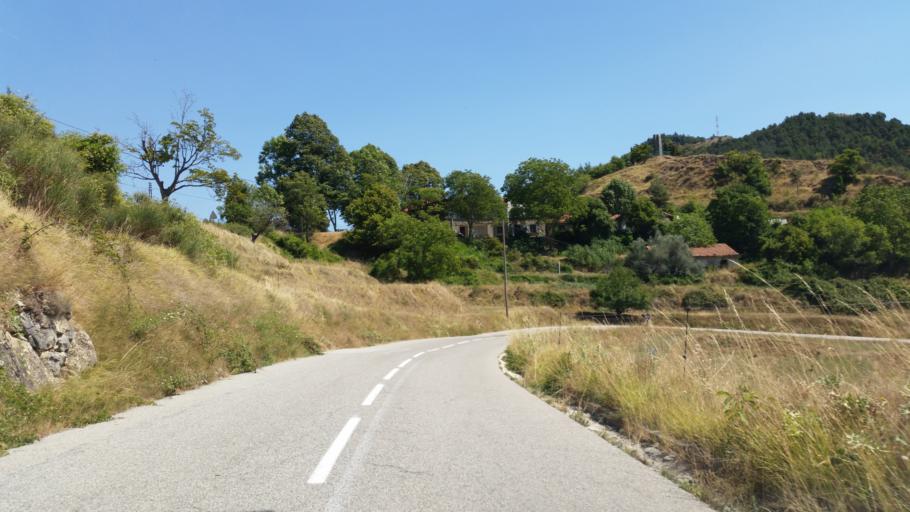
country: FR
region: Provence-Alpes-Cote d'Azur
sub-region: Departement des Alpes-Maritimes
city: Breil-sur-Roya
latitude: 43.9234
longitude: 7.4752
